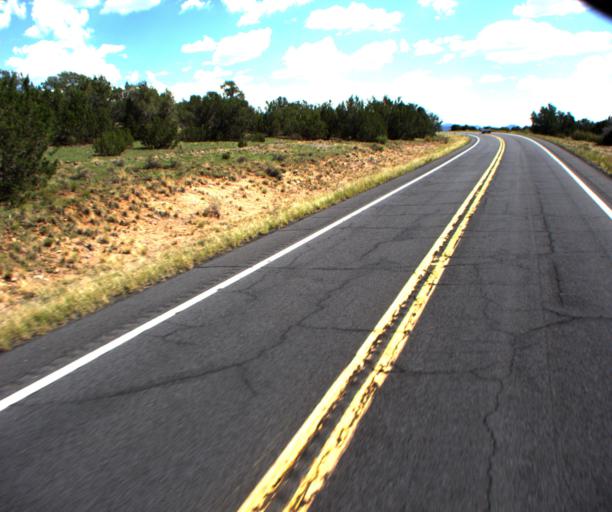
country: US
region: Arizona
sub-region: Coconino County
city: Williams
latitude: 35.4794
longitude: -112.1772
